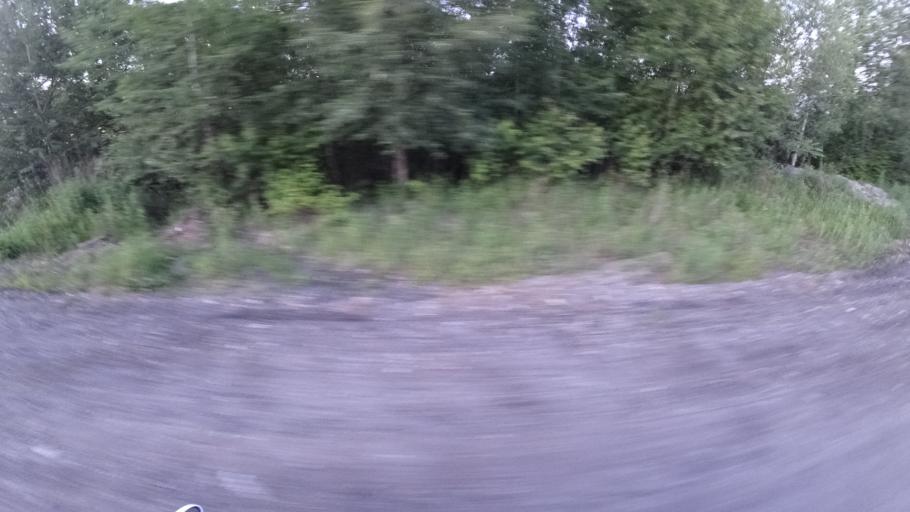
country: RU
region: Khabarovsk Krai
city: Khor
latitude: 47.8540
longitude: 134.9429
